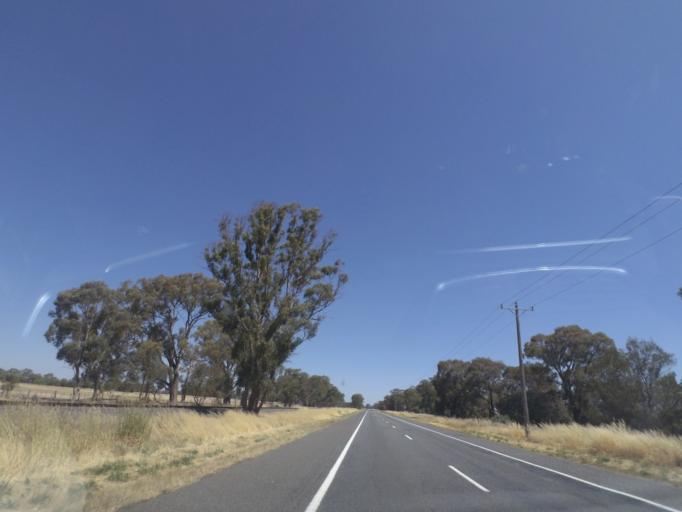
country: AU
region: Victoria
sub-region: Greater Shepparton
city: Shepparton
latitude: -36.2145
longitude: 145.4319
